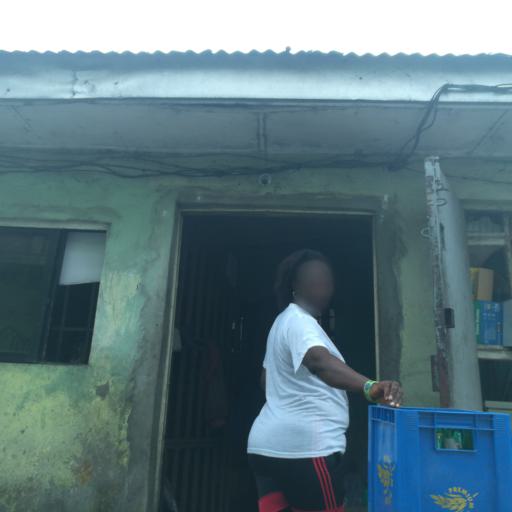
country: NG
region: Rivers
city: Port Harcourt
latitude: 4.7484
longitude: 7.0074
